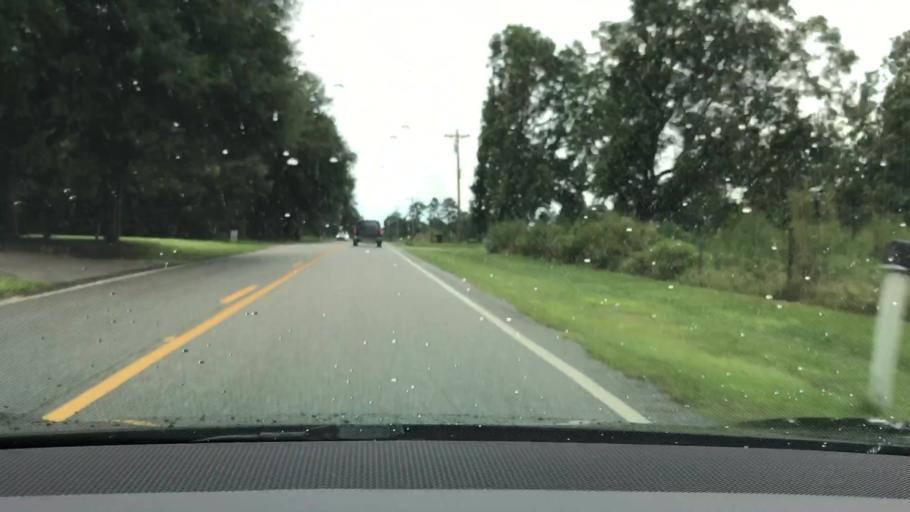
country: US
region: Alabama
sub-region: Geneva County
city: Samson
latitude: 31.0807
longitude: -86.1057
